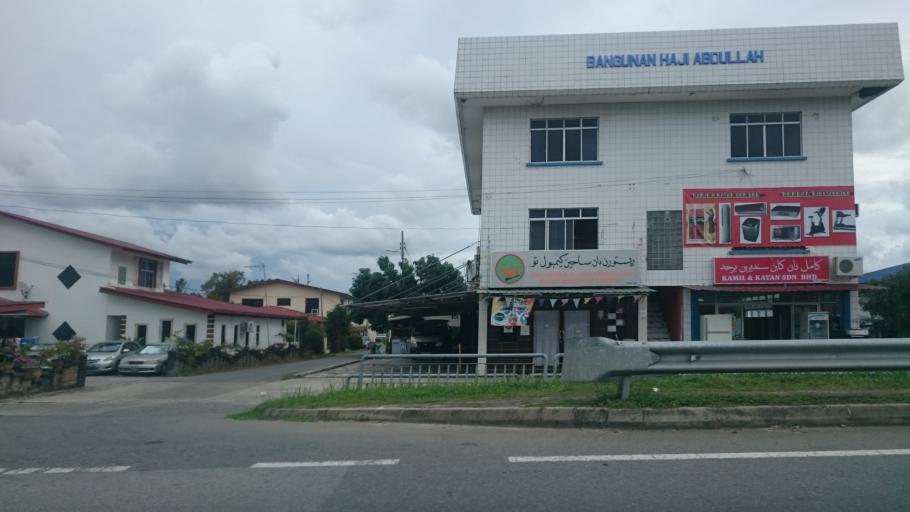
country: BN
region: Brunei and Muara
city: Bandar Seri Begawan
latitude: 4.8887
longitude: 114.8439
